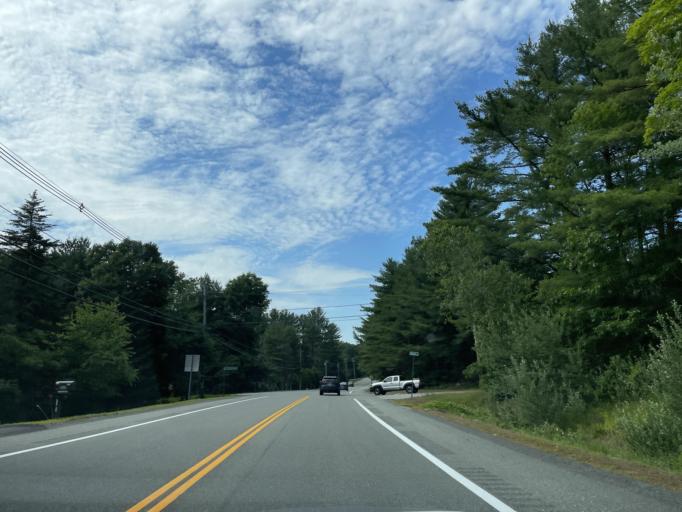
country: US
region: Rhode Island
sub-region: Kent County
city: West Greenwich
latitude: 41.6437
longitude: -71.6911
